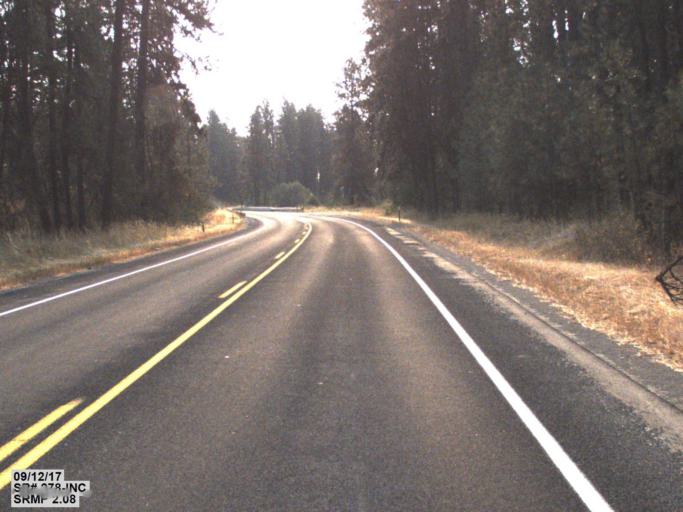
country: US
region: Washington
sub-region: Spokane County
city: Veradale
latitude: 47.4414
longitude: -117.1067
